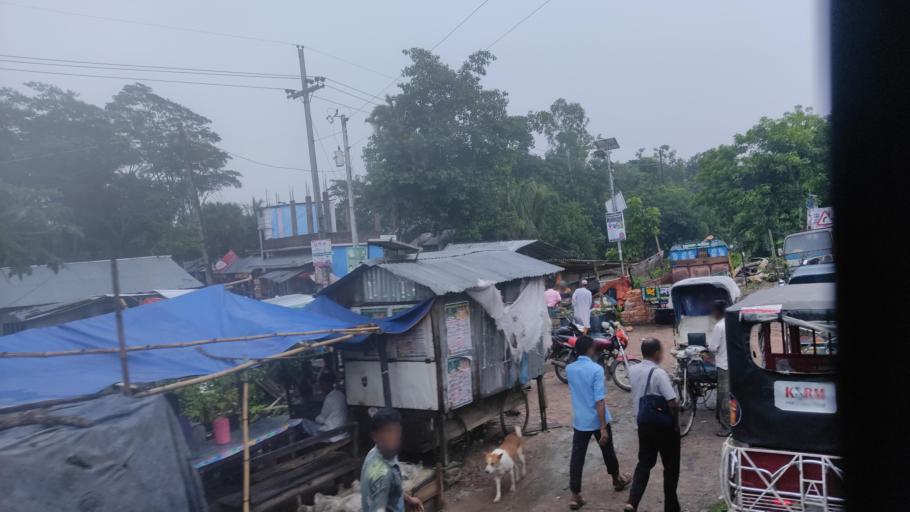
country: BD
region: Barisal
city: Bhandaria
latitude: 22.2936
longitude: 90.3252
